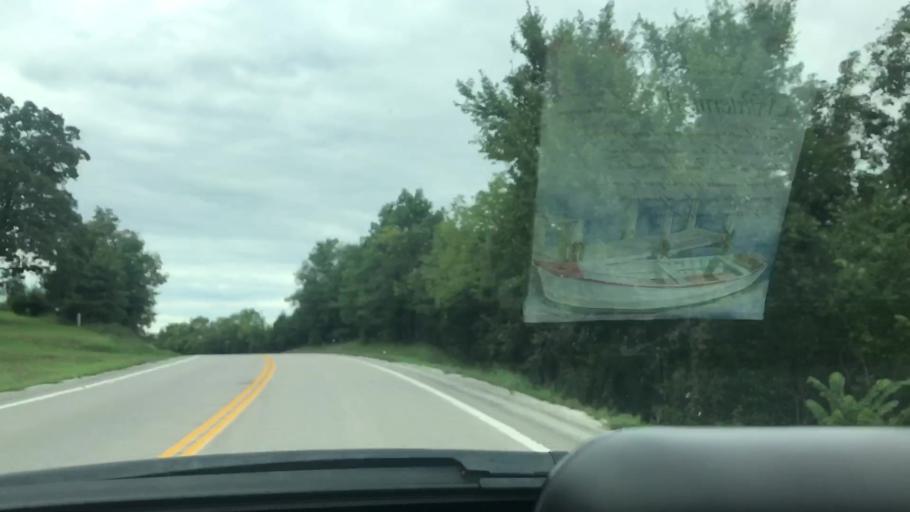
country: US
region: Missouri
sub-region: Benton County
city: Warsaw
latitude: 38.1693
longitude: -93.3102
